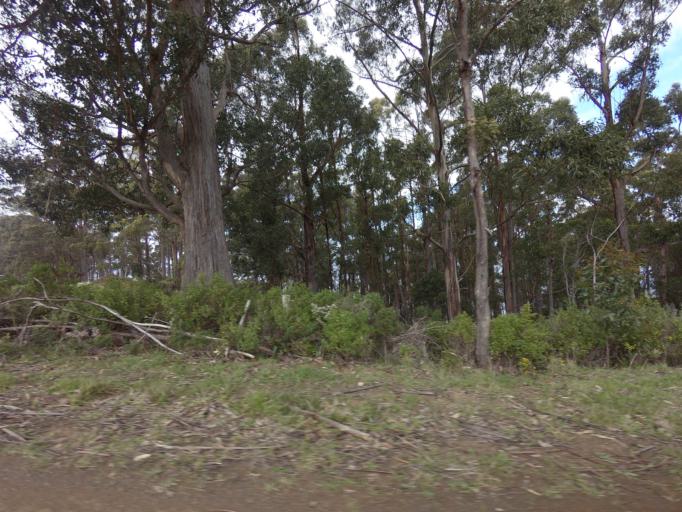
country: AU
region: Tasmania
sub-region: Huon Valley
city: Cygnet
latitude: -43.4142
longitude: 147.0171
